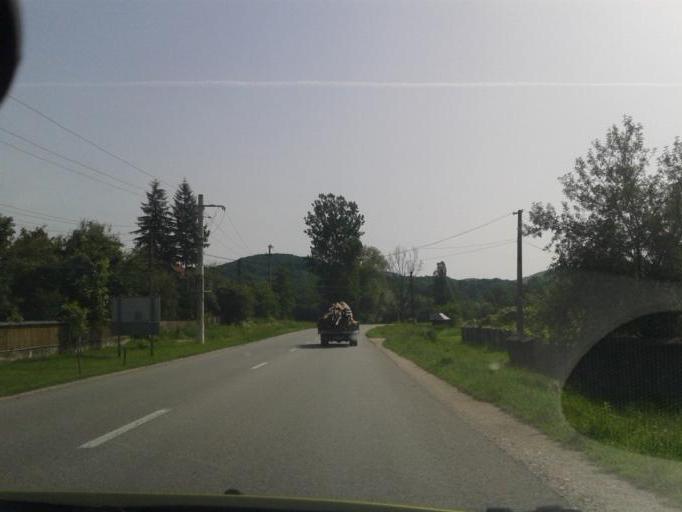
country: RO
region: Valcea
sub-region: Comuna Stoenesti
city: Stoenesti
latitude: 45.1137
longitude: 24.1620
